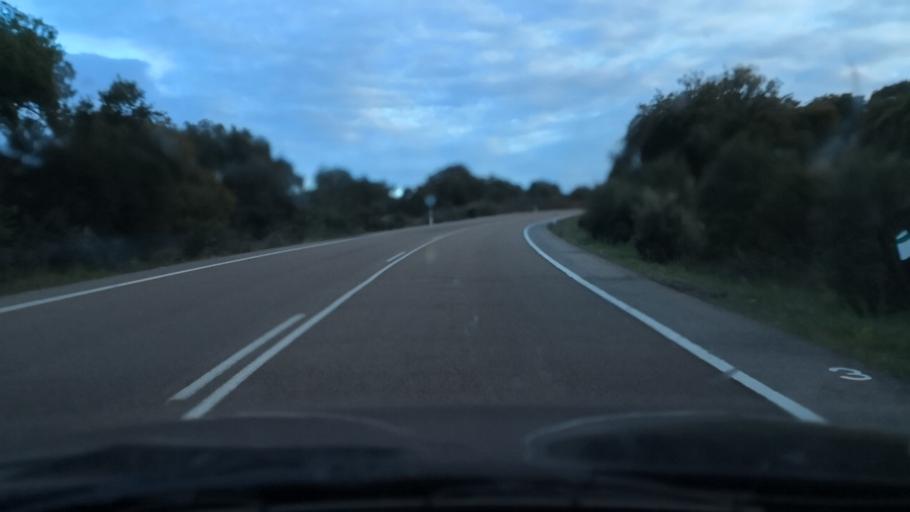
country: ES
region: Extremadura
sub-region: Provincia de Badajoz
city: Puebla de Obando
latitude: 39.2454
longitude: -6.5579
